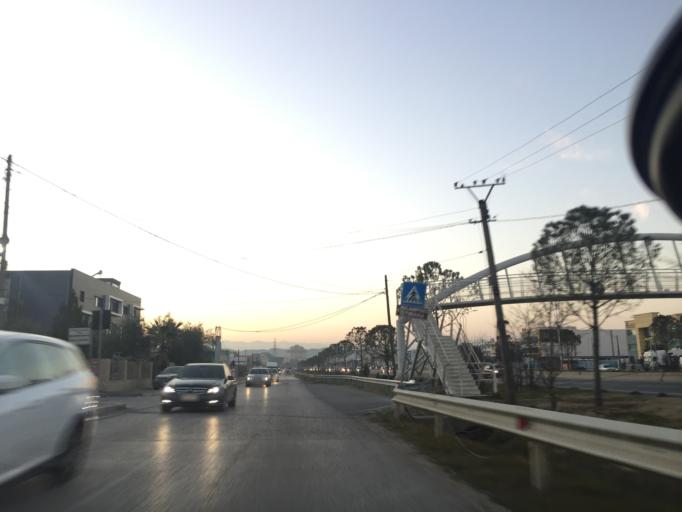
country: AL
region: Tirane
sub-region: Rrethi i Tiranes
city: Kashar
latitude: 41.3613
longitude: 19.7216
